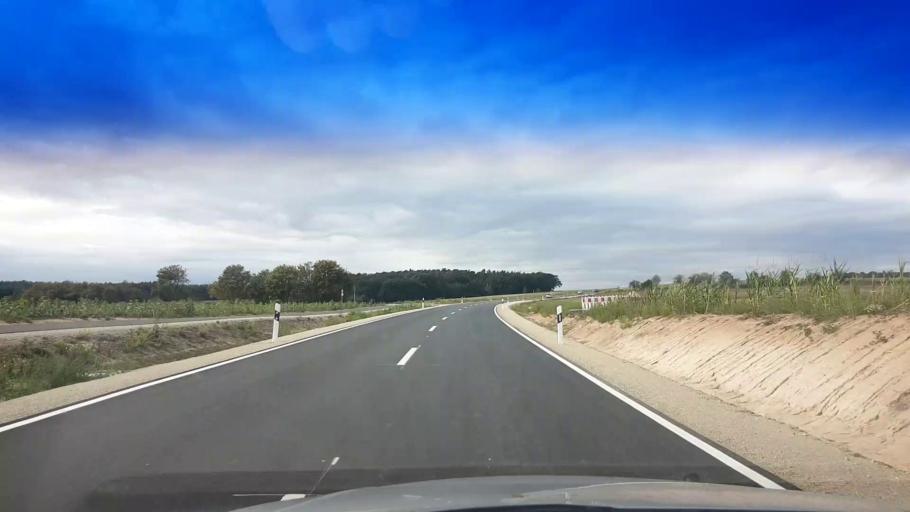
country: DE
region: Bavaria
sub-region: Upper Franconia
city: Frensdorf
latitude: 49.7961
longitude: 10.8800
